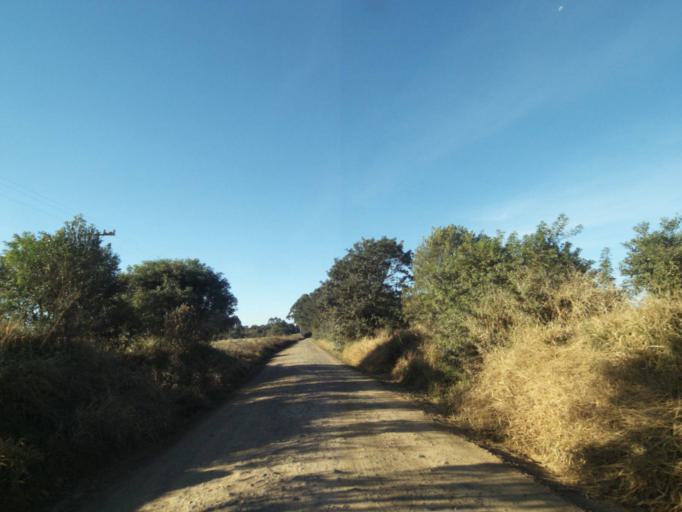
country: BR
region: Parana
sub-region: Tibagi
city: Tibagi
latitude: -24.5453
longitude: -50.6174
